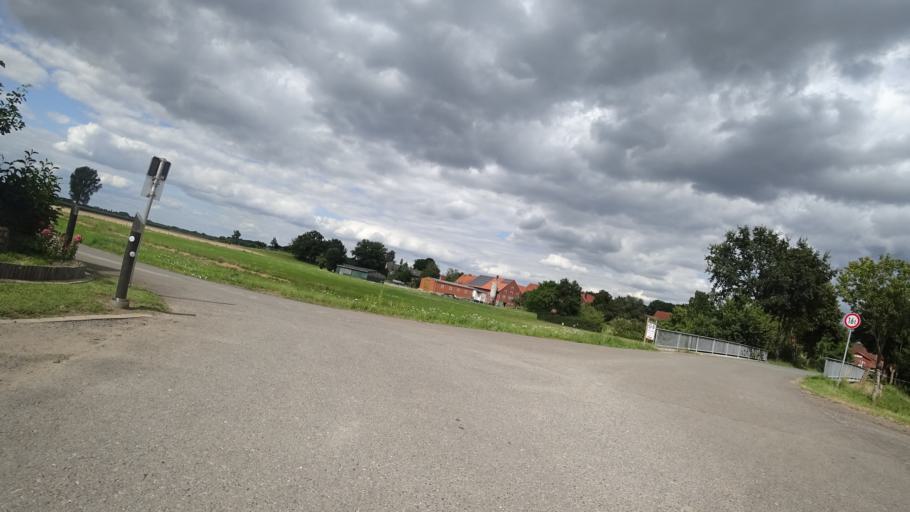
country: DE
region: Lower Saxony
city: Raddestorf
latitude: 52.4323
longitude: 9.0311
